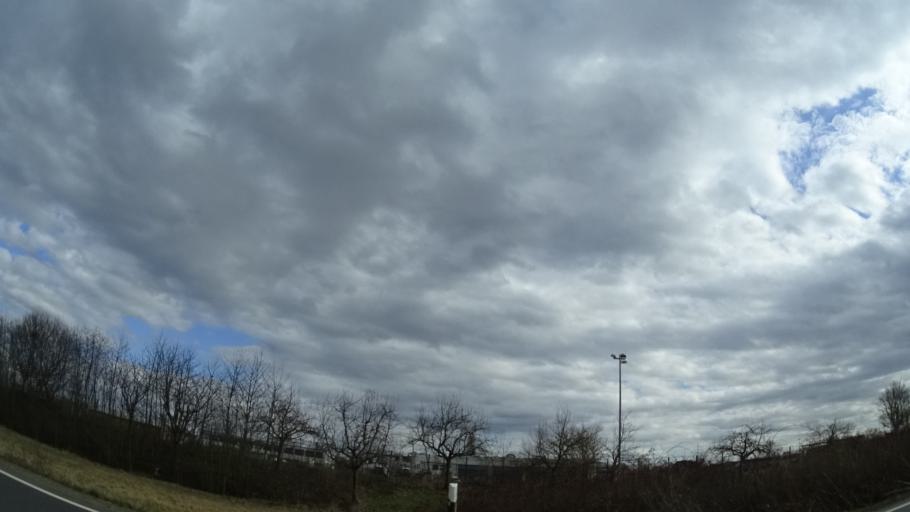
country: DE
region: Hesse
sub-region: Regierungsbezirk Darmstadt
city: Riedstadt
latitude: 49.8325
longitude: 8.4816
